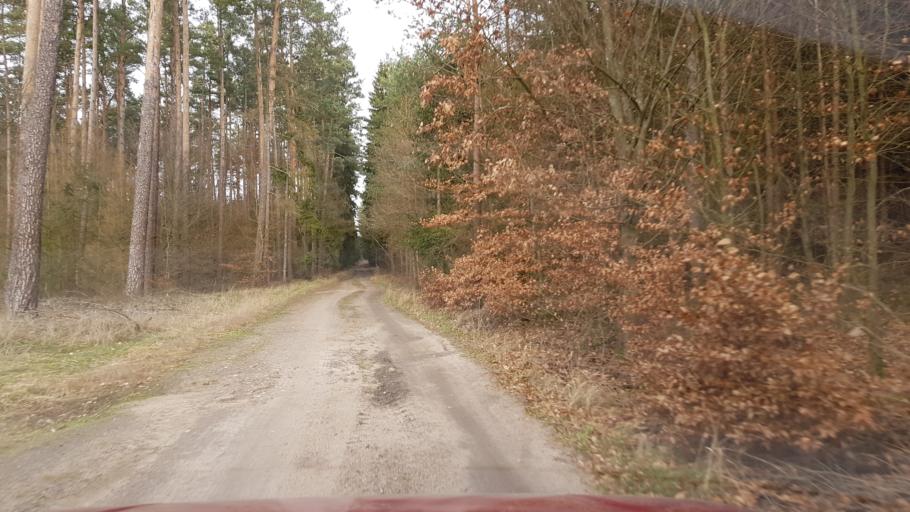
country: PL
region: Lubusz
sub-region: Powiat strzelecko-drezdenecki
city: Strzelce Krajenskie
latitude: 52.9082
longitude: 15.4075
